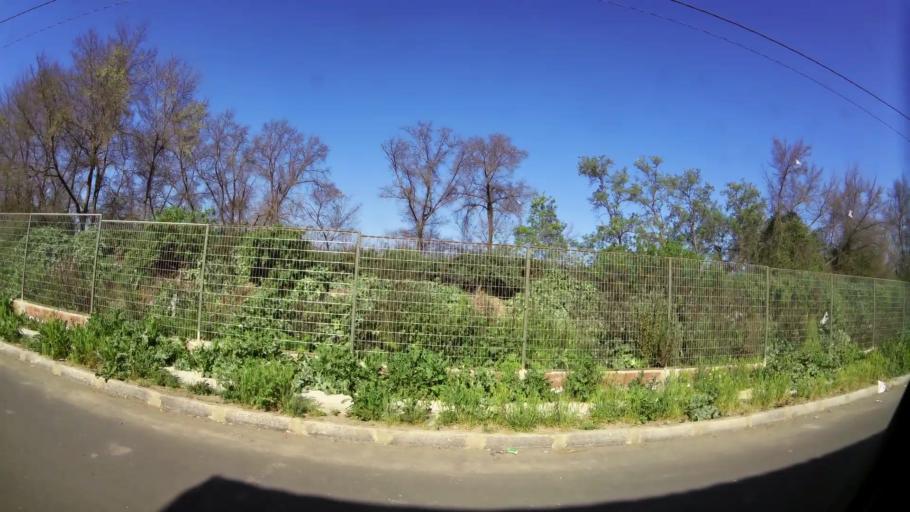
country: CL
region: Santiago Metropolitan
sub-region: Provincia de Talagante
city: Penaflor
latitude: -33.6168
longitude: -70.8771
